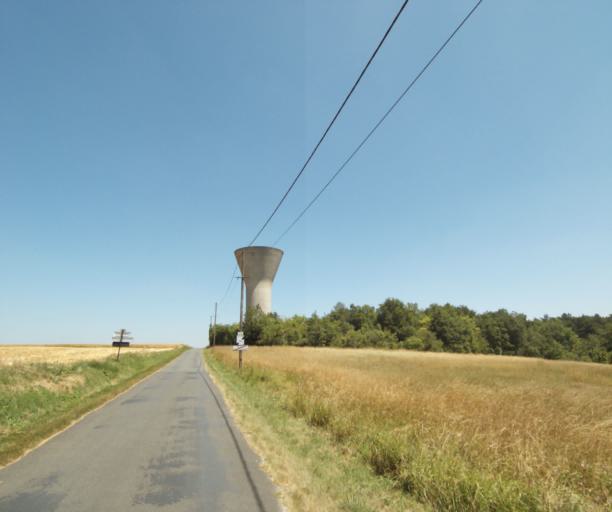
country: FR
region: Centre
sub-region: Departement du Loiret
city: Malesherbes
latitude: 48.2997
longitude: 2.4423
